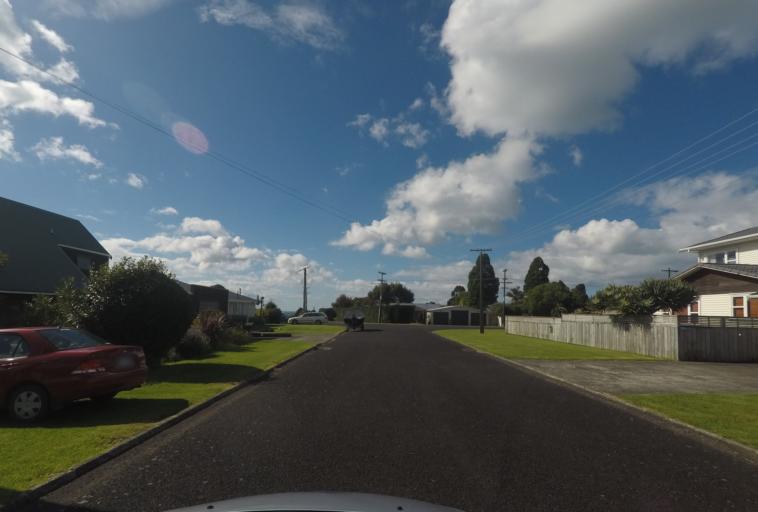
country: NZ
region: Bay of Plenty
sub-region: Western Bay of Plenty District
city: Waihi Beach
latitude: -37.4128
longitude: 175.9377
